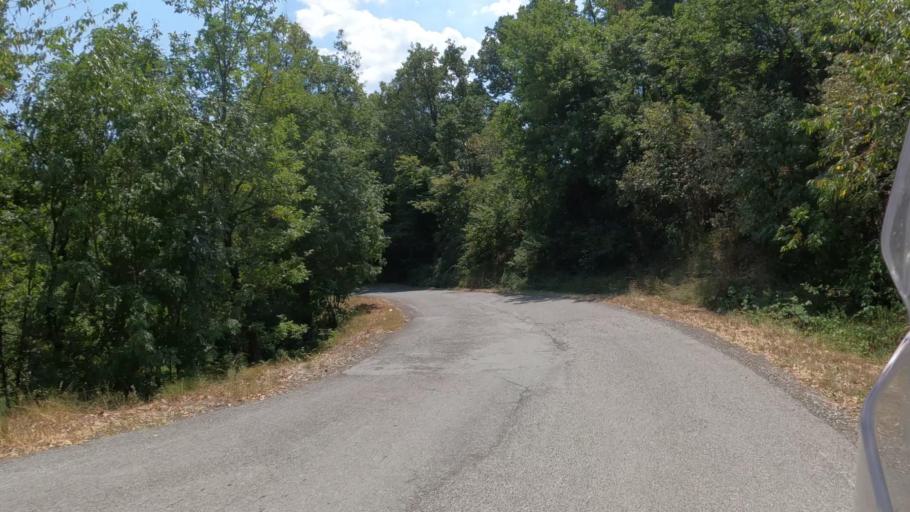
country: IT
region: Piedmont
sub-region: Provincia di Alessandria
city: Cassinelle-Concentrico
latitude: 44.5794
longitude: 8.5399
